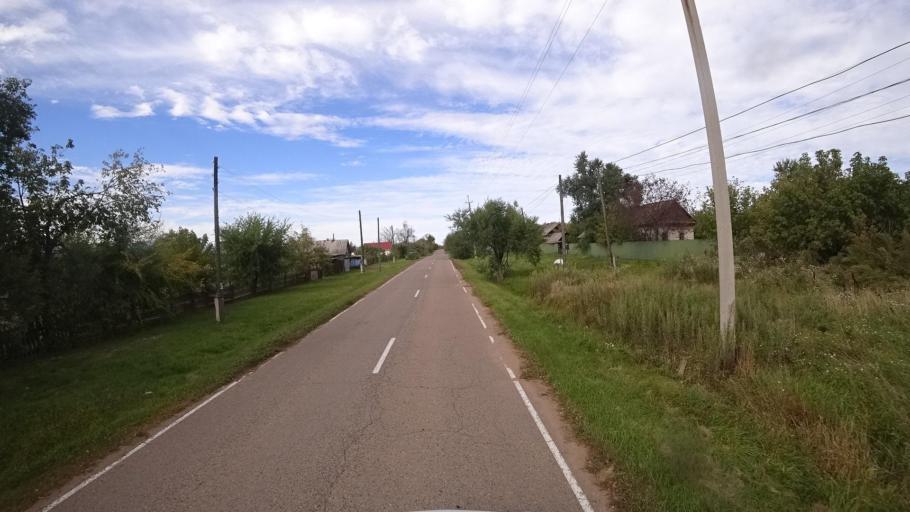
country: RU
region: Primorskiy
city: Dostoyevka
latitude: 44.3224
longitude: 133.4764
